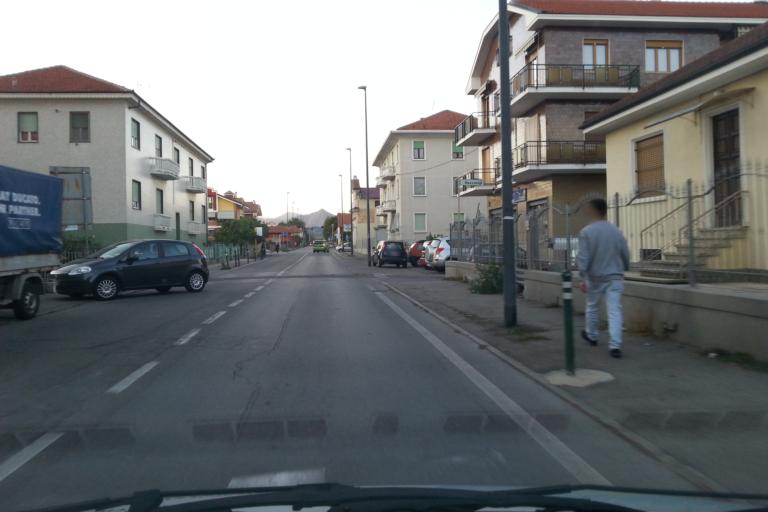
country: IT
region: Piedmont
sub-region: Provincia di Torino
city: Piossasco
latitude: 44.9905
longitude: 7.4682
